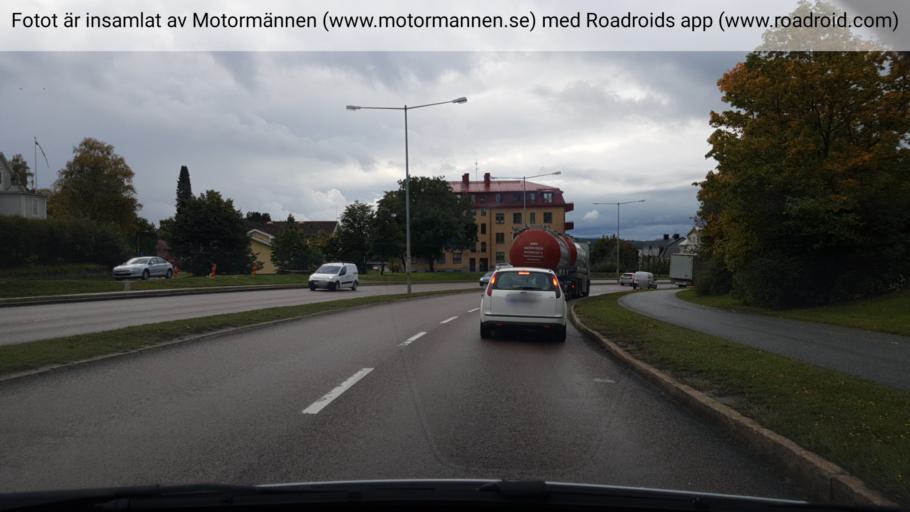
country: SE
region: Vaesternorrland
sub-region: OErnskoeldsviks Kommun
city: Ornskoldsvik
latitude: 63.2936
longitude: 18.7215
